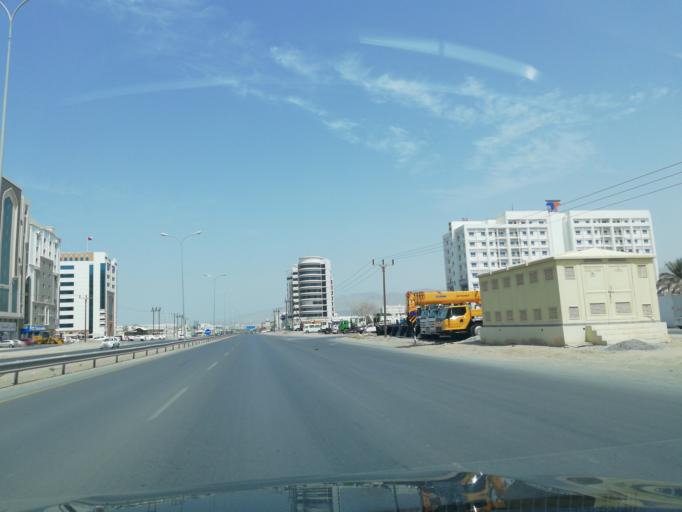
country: OM
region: Muhafazat Masqat
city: Bawshar
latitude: 23.5826
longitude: 58.3707
